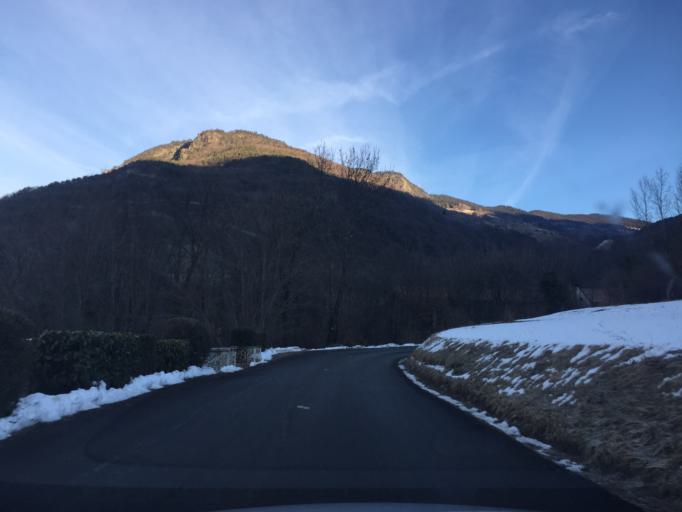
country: FR
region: Rhone-Alpes
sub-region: Departement de la Savoie
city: Aigueblanche
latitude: 45.5219
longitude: 6.4917
